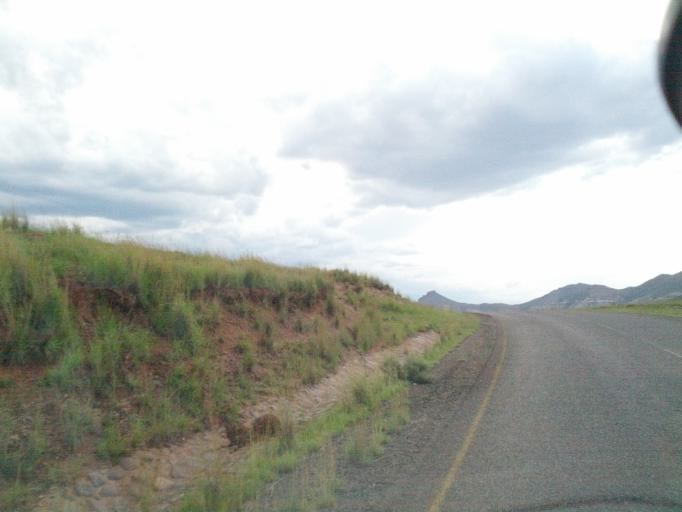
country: LS
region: Qacha's Nek
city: Qacha's Nek
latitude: -30.0507
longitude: 28.4953
